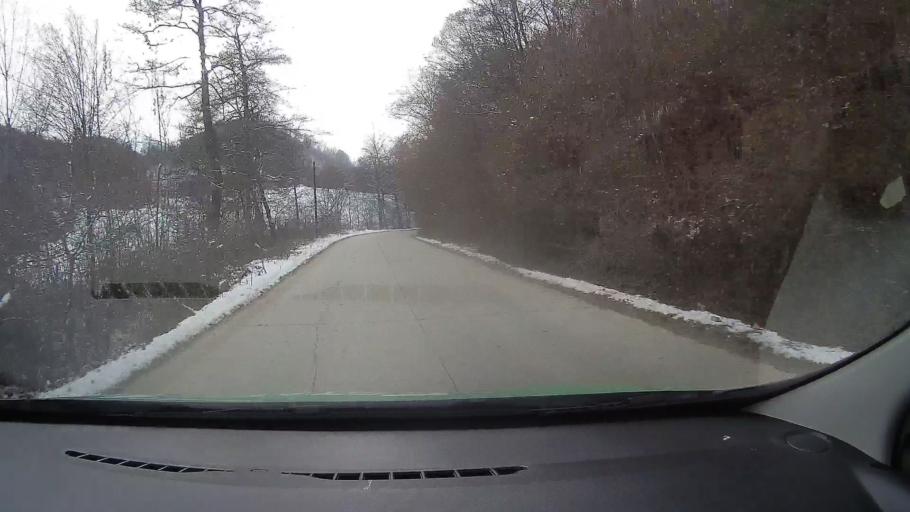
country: RO
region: Alba
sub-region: Oras Zlatna
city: Zlatna
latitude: 46.1107
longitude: 23.1983
